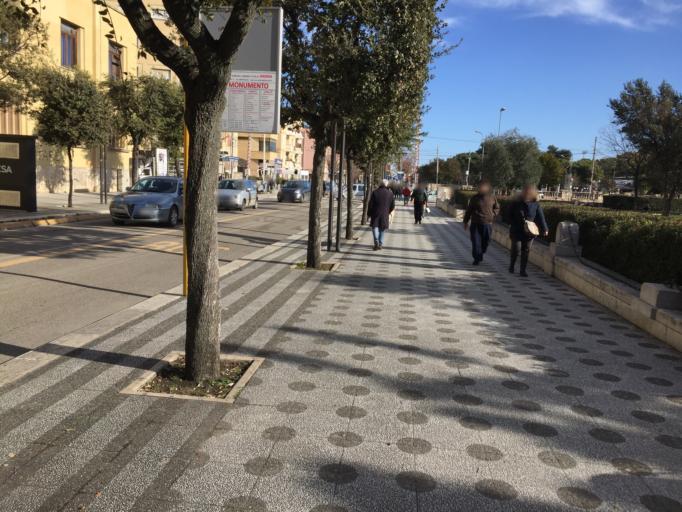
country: IT
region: Apulia
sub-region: Provincia di Barletta - Andria - Trani
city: Andria
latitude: 41.2308
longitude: 16.3036
